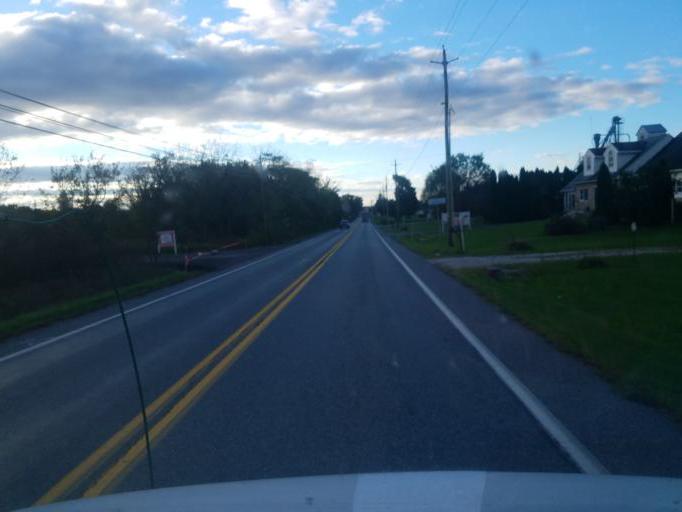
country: US
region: Pennsylvania
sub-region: Adams County
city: Lake Meade
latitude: 39.9343
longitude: -77.0604
